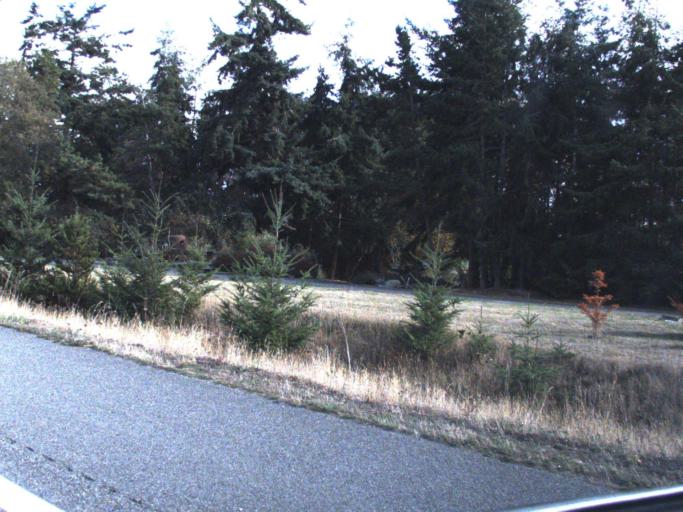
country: US
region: Washington
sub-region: Island County
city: Oak Harbor
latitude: 48.2649
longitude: -122.6780
